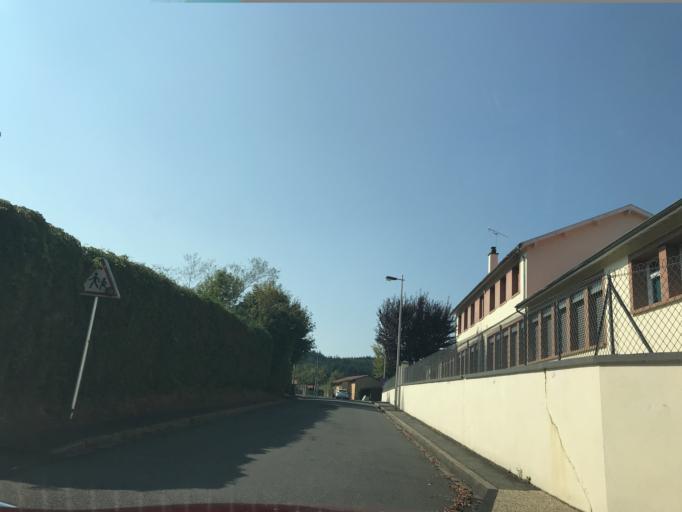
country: FR
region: Auvergne
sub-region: Departement du Puy-de-Dome
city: Celles-sur-Durolle
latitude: 45.8564
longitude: 3.6357
